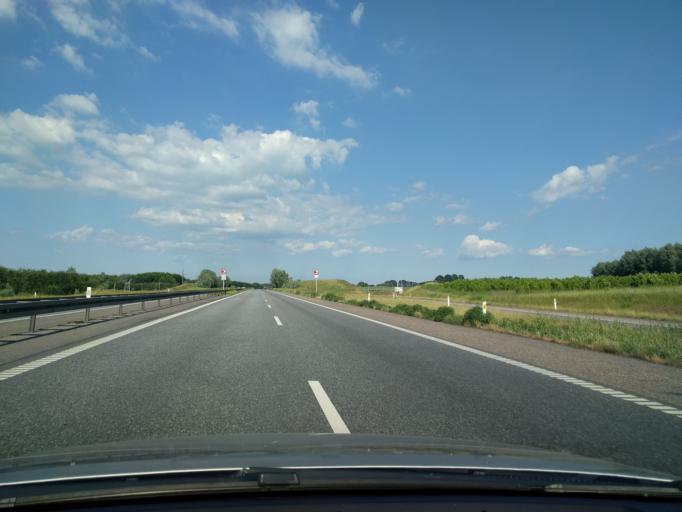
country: DK
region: Zealand
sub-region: Slagelse Kommune
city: Slagelse
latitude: 55.3802
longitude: 11.3248
